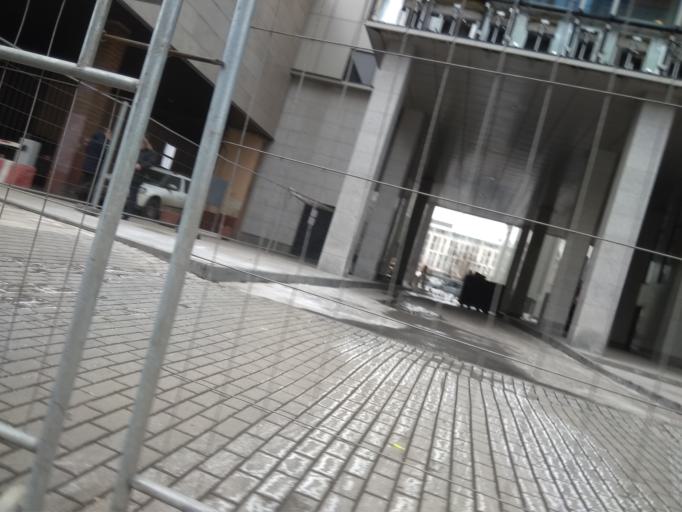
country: RU
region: Moscow
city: Moscow
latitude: 55.7739
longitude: 37.6044
